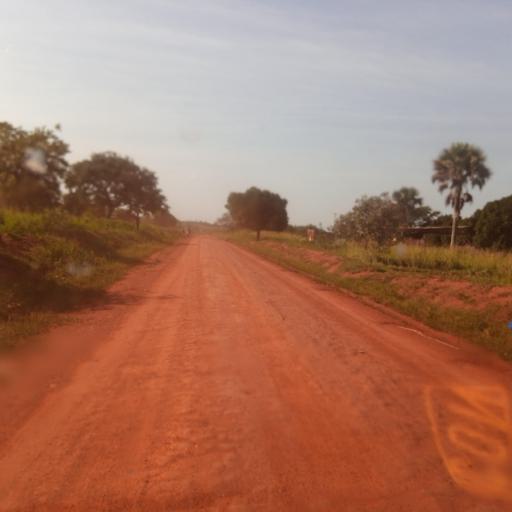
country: UG
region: Northern Region
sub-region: Kitgum District
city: Kitgum
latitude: 3.1100
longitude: 32.9145
